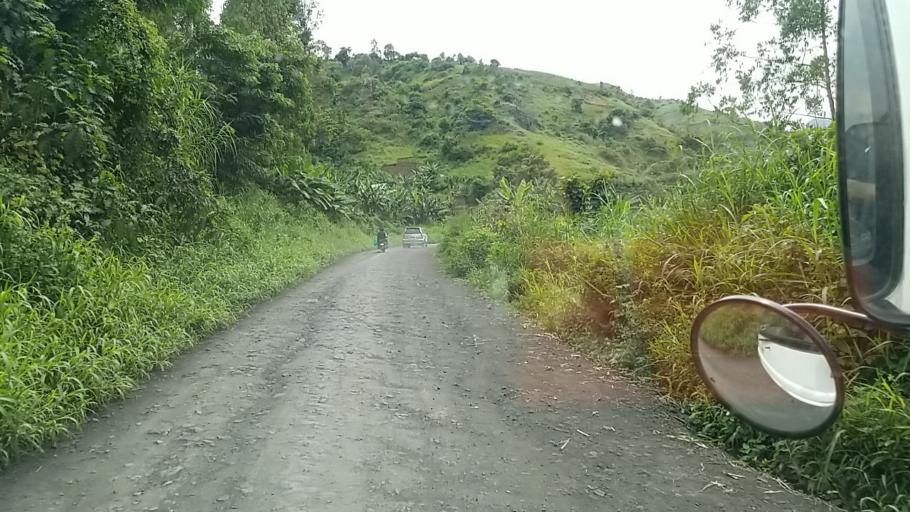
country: CD
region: Nord Kivu
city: Sake
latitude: -1.7366
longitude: 29.0073
